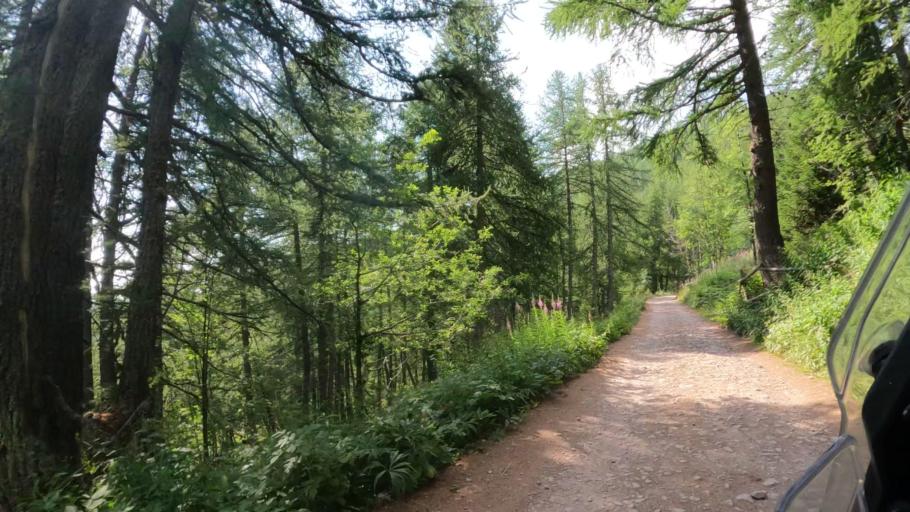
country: IT
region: Piedmont
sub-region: Provincia di Cuneo
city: Briga Alta
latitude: 44.1218
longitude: 7.6912
